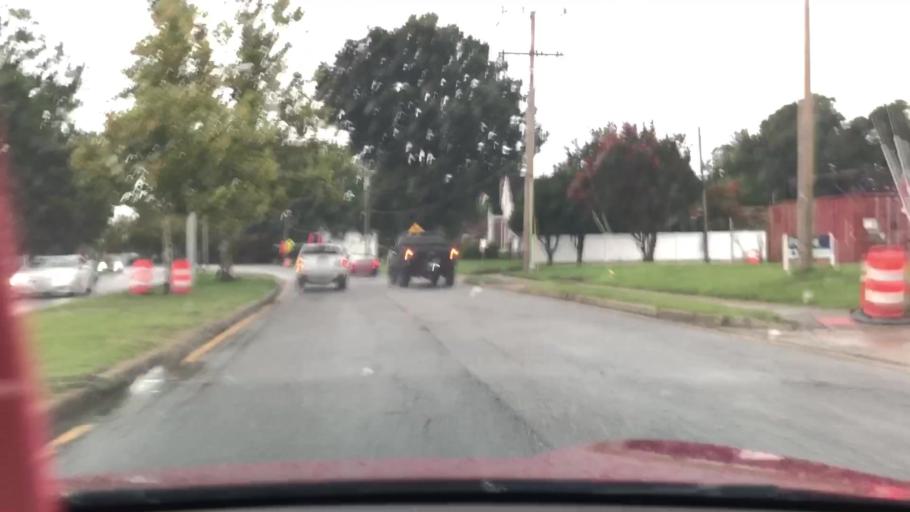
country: US
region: Virginia
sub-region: City of Chesapeake
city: Chesapeake
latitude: 36.8451
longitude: -76.1906
